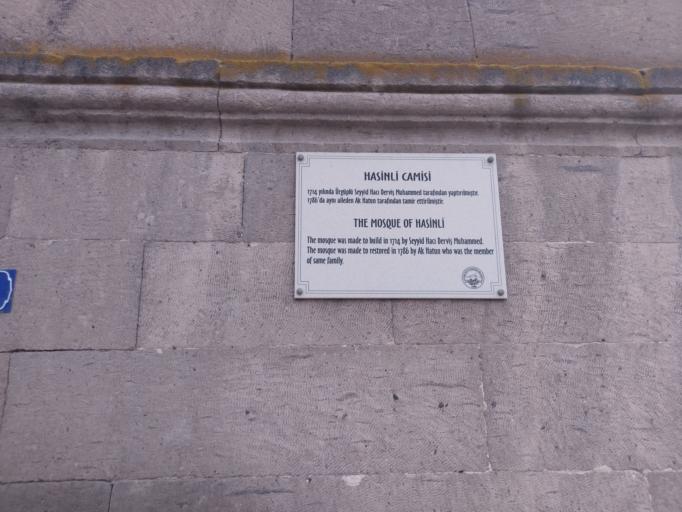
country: TR
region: Kayseri
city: Kayseri
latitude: 38.7146
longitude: 35.4901
